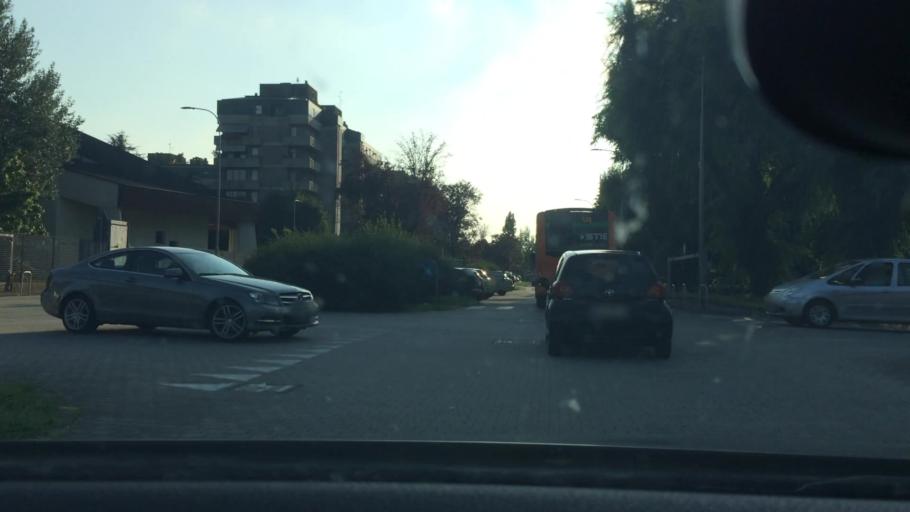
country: IT
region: Lombardy
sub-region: Citta metropolitana di Milano
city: Pregnana Milanese
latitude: 45.5359
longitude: 9.0190
